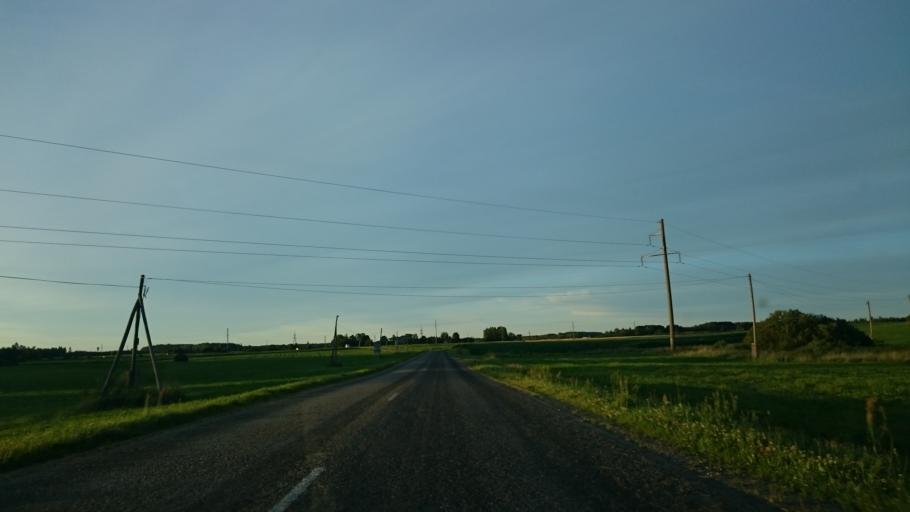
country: LV
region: Saldus Rajons
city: Saldus
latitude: 56.6808
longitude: 22.4998
